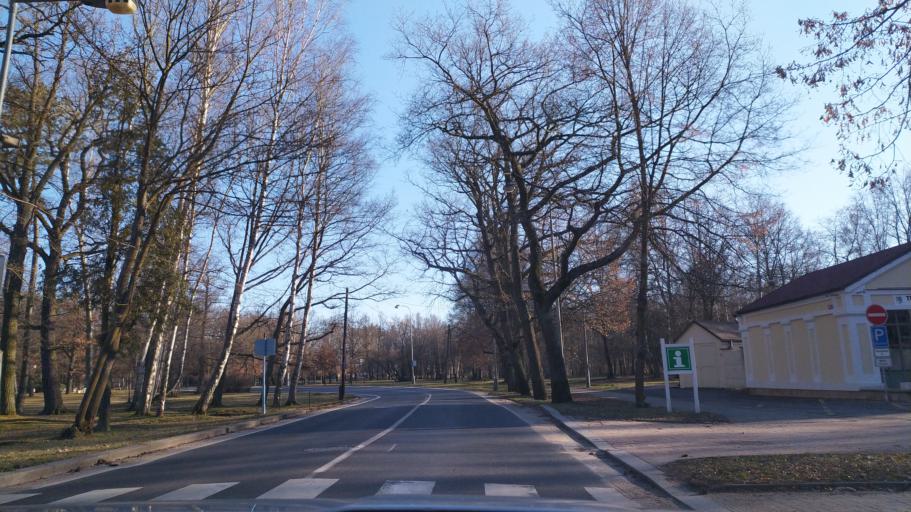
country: CZ
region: Karlovarsky
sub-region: Okres Cheb
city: Frantiskovy Lazne
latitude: 50.1170
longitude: 12.3496
